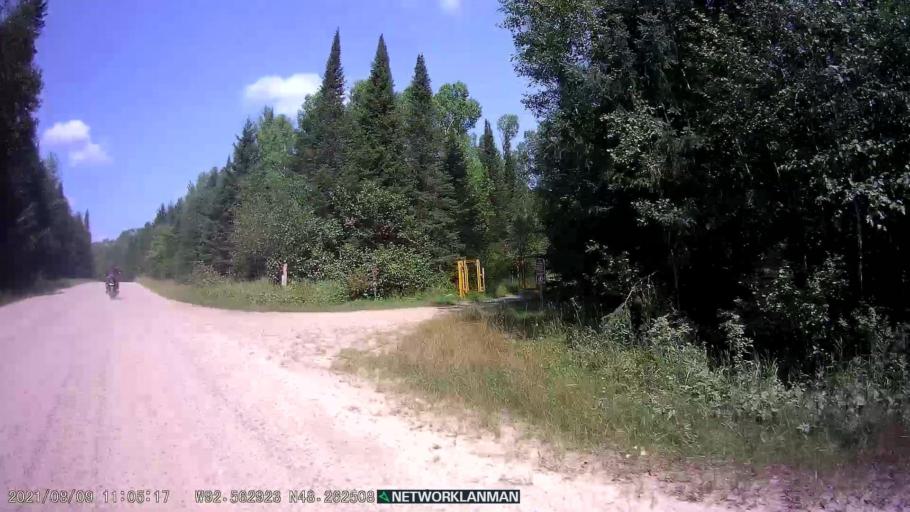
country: US
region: Minnesota
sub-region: Saint Louis County
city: Parkville
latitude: 48.2626
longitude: -92.5630
